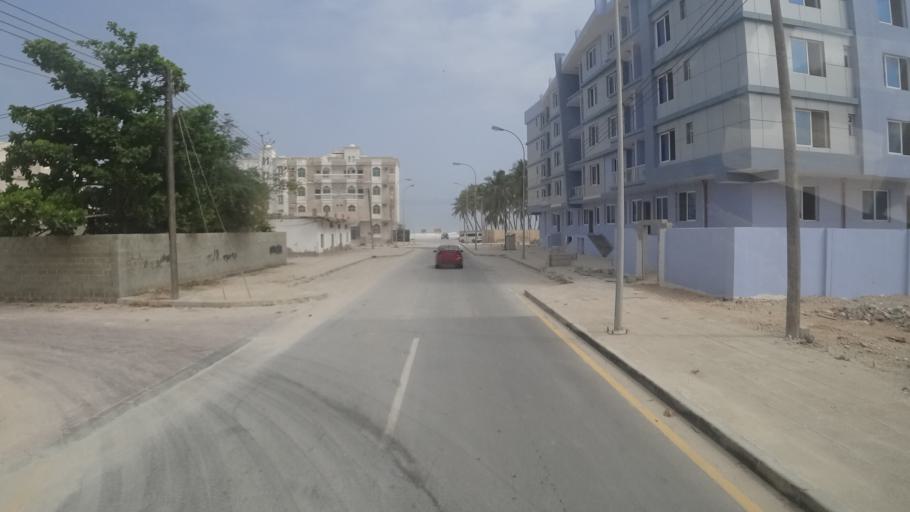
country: OM
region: Zufar
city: Salalah
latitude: 17.0102
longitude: 54.1574
